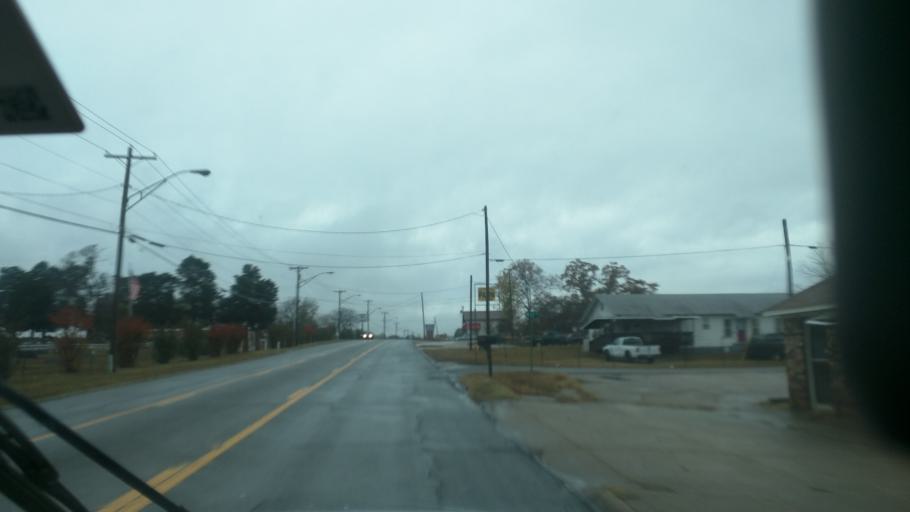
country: US
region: Arkansas
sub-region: Franklin County
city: Ozark
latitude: 35.4881
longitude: -93.8376
